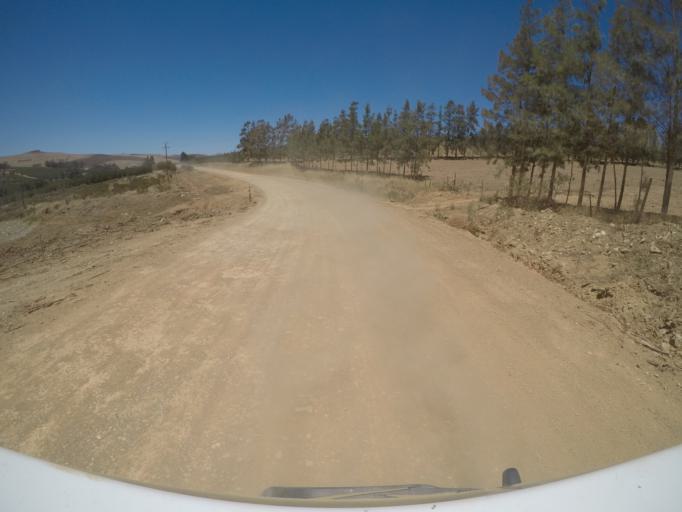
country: ZA
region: Western Cape
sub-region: Overberg District Municipality
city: Grabouw
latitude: -34.0911
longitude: 19.1922
